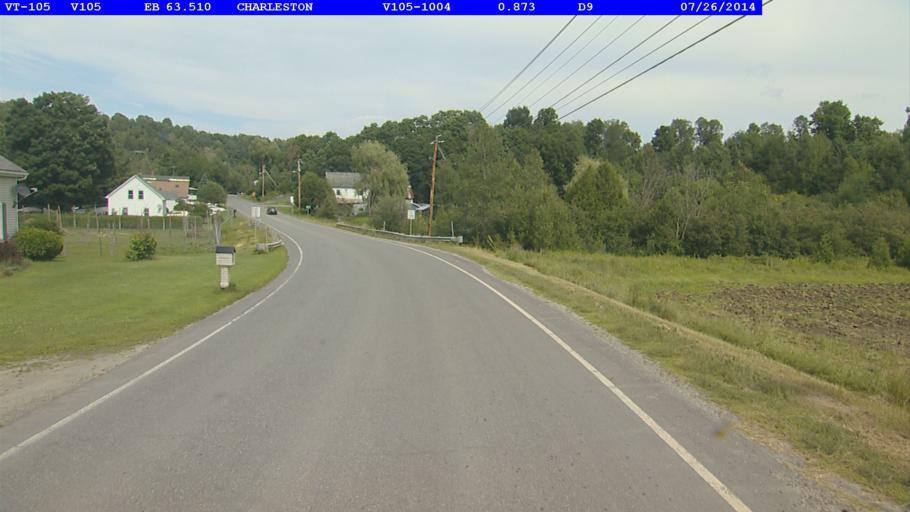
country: US
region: Vermont
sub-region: Orleans County
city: Newport
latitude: 44.8977
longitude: -72.0632
